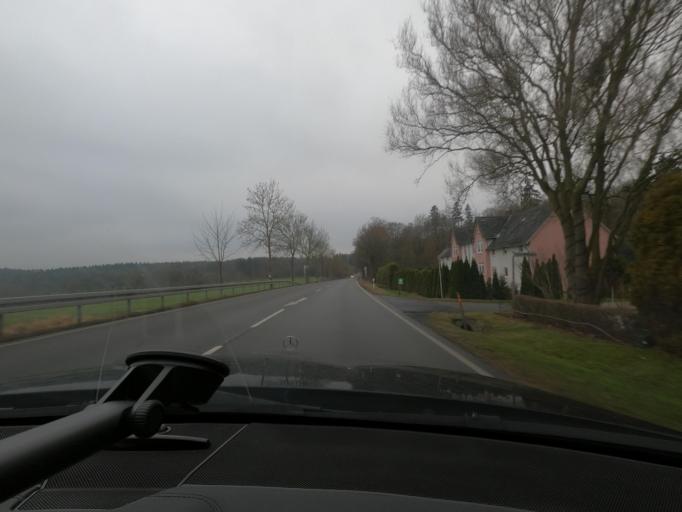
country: DE
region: Hesse
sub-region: Regierungsbezirk Kassel
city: Bad Arolsen
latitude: 51.4187
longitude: 9.0189
